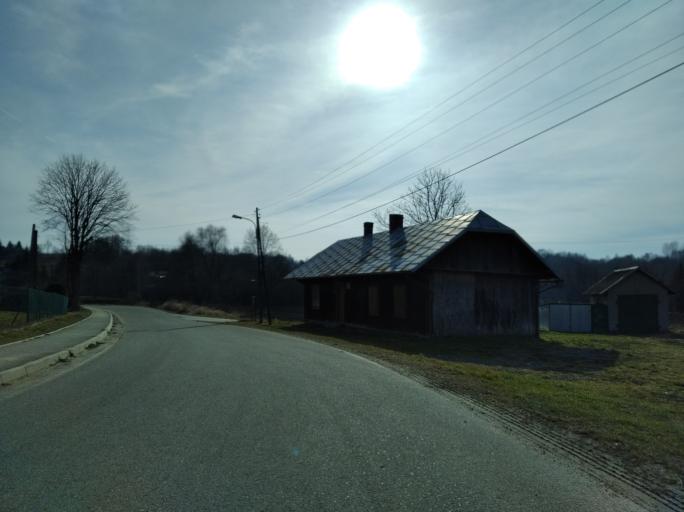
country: PL
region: Subcarpathian Voivodeship
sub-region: Powiat brzozowski
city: Gorki
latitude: 49.6459
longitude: 22.0398
